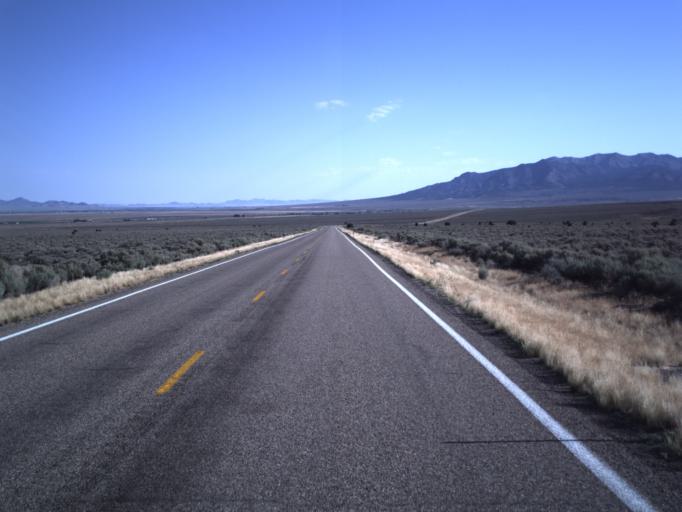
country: US
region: Utah
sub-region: Beaver County
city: Milford
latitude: 38.1421
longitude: -112.9599
